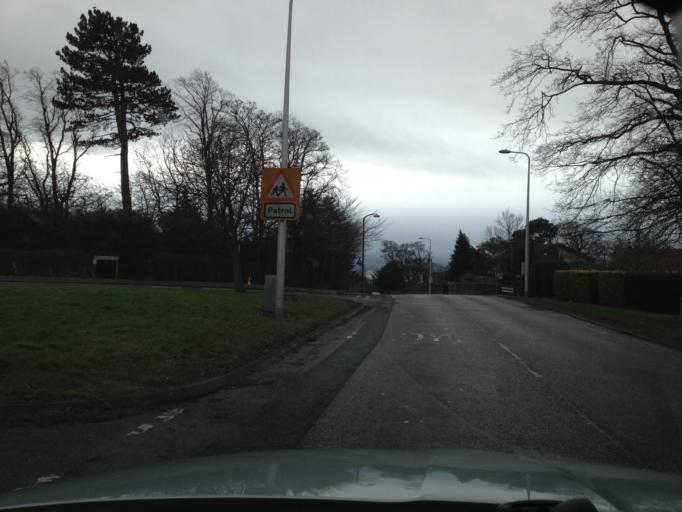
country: GB
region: Scotland
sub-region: Edinburgh
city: Colinton
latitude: 55.9490
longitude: -3.2793
